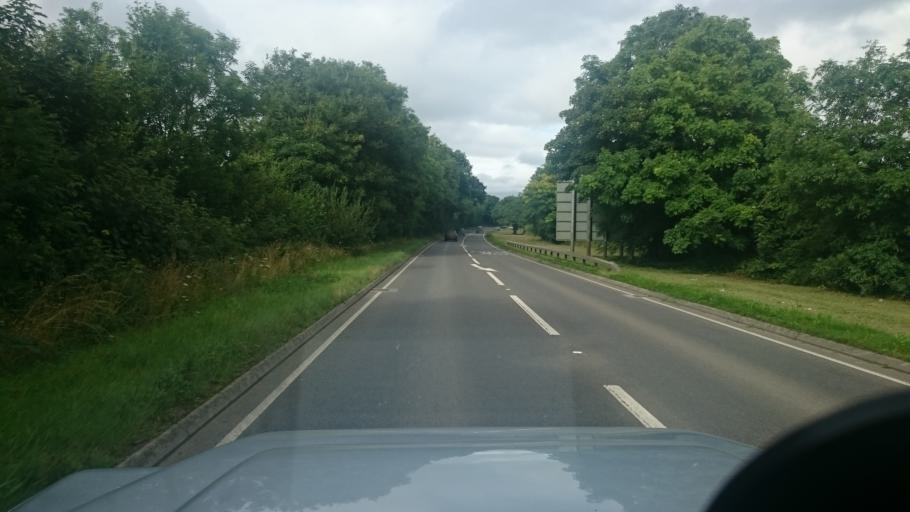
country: GB
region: Wales
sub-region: Pembrokeshire
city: Narberth
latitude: 51.8132
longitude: -4.7433
